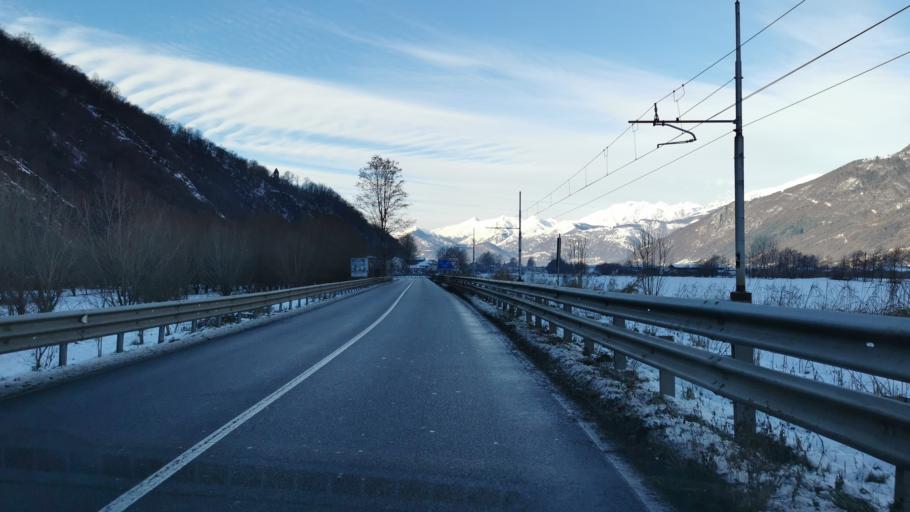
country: IT
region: Lombardy
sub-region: Provincia di Sondrio
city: Traona
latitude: 46.1357
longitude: 9.5150
